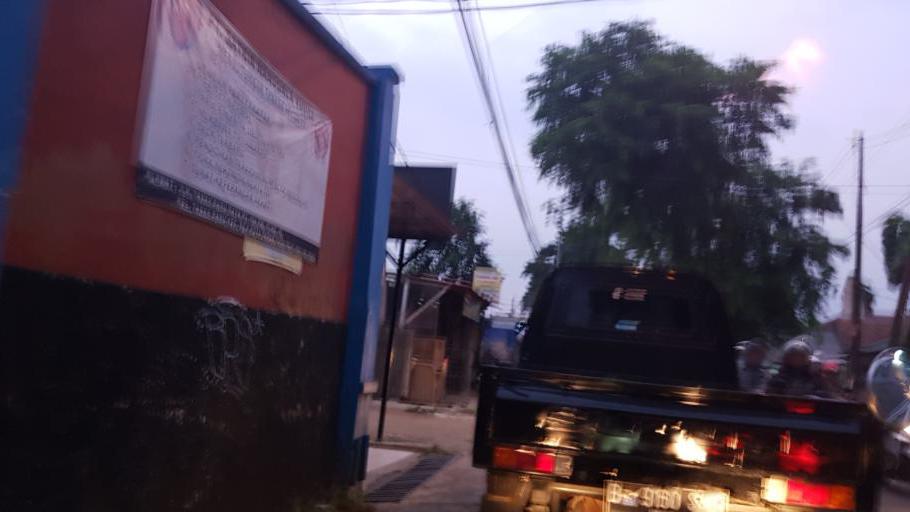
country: ID
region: West Java
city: Depok
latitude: -6.3665
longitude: 106.8077
